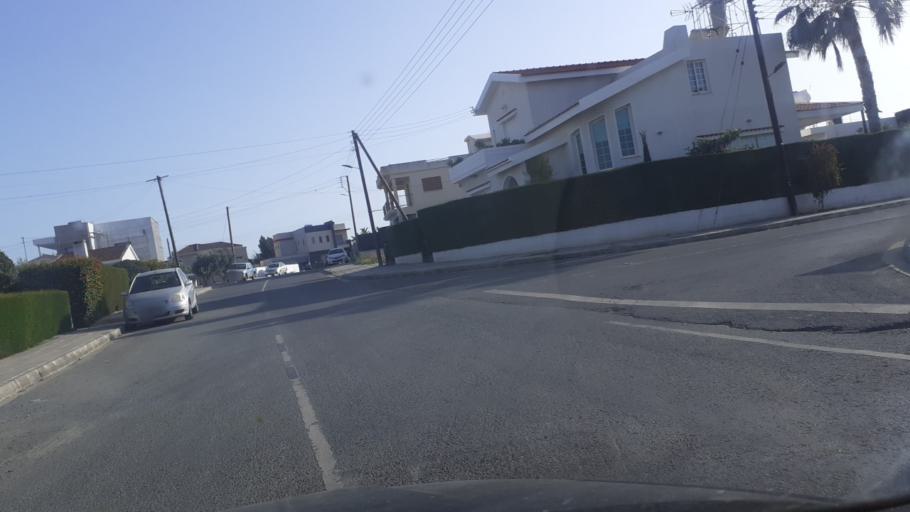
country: CY
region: Larnaka
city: Kolossi
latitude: 34.6623
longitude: 32.9578
